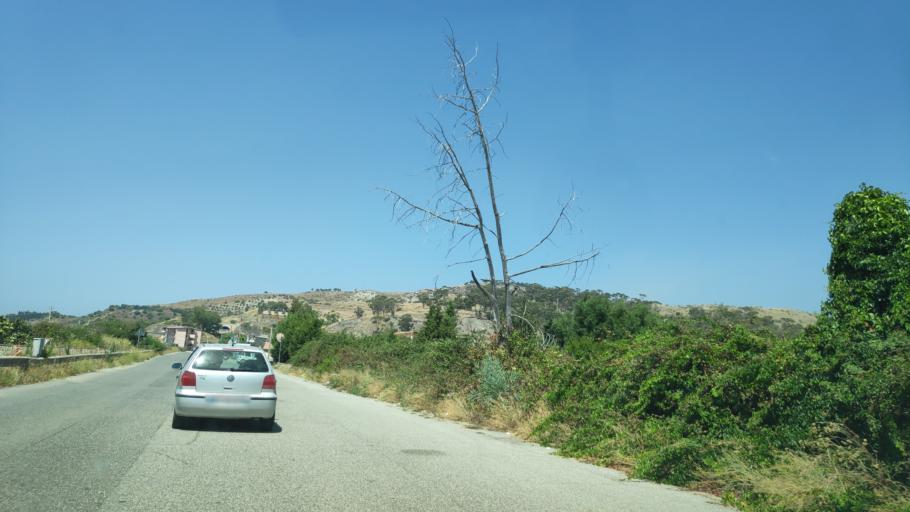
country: IT
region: Calabria
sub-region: Provincia di Reggio Calabria
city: Palizzi Marina
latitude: 37.9233
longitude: 15.9526
